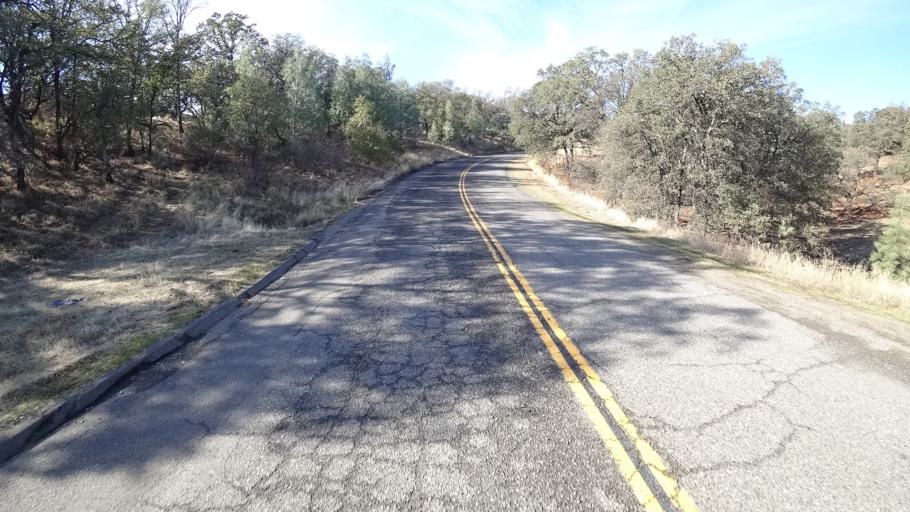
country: US
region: California
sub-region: Shasta County
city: Anderson
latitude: 40.4008
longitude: -122.4066
